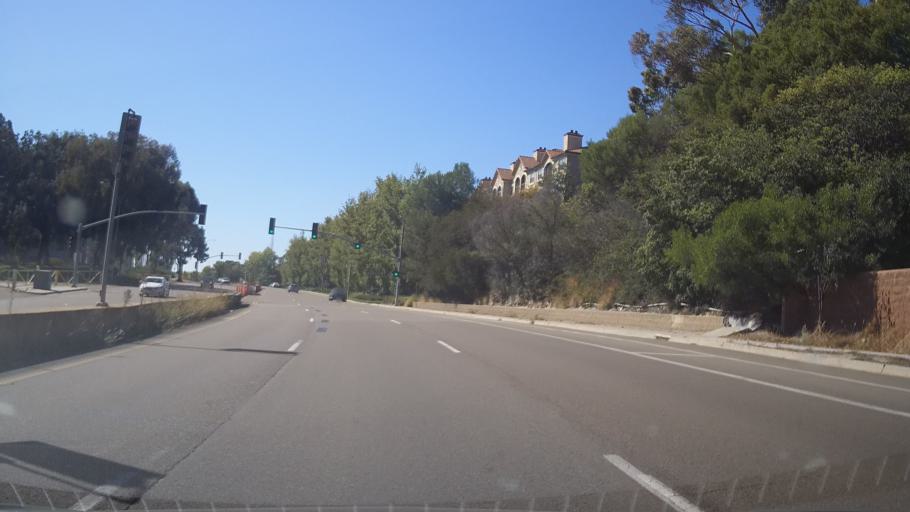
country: US
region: California
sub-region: San Diego County
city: San Diego
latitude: 32.7861
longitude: -117.1243
